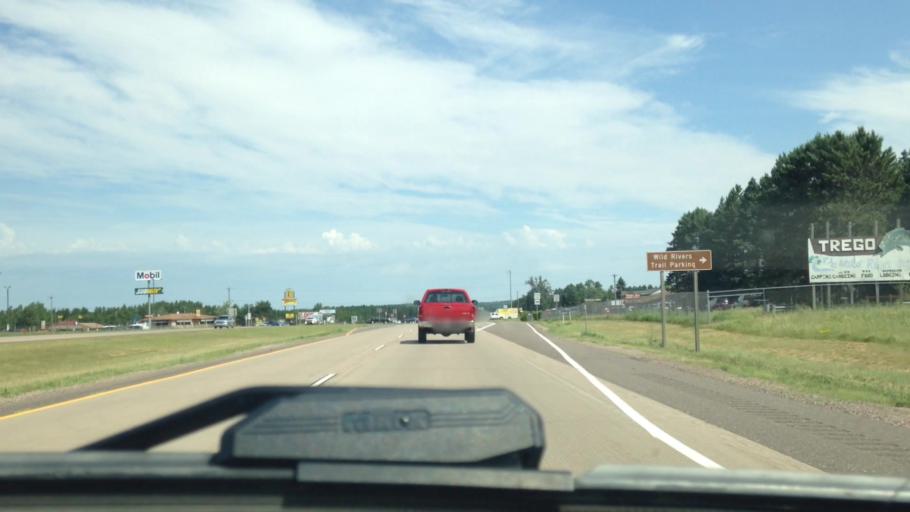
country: US
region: Wisconsin
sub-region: Washburn County
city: Spooner
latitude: 45.8973
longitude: -91.8277
